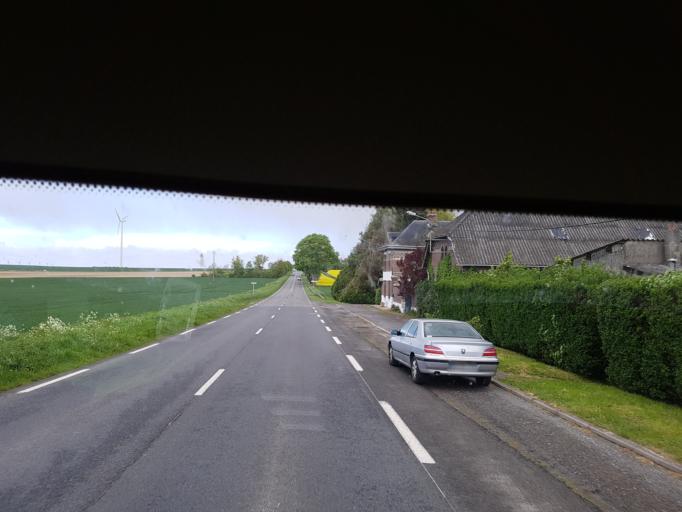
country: FR
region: Picardie
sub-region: Departement de l'Aisne
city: Saint-Quentin
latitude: 49.8936
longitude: 3.2642
